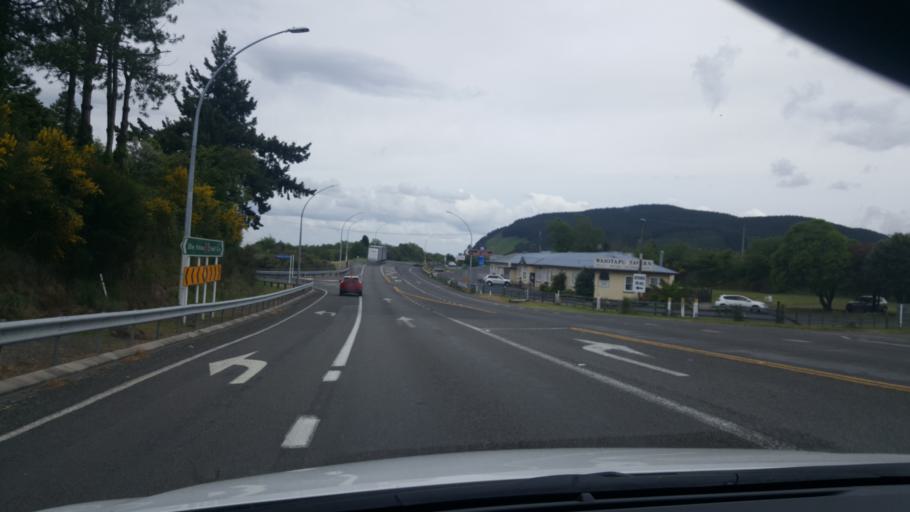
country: NZ
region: Bay of Plenty
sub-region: Rotorua District
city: Rotorua
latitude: -38.3390
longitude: 176.3639
